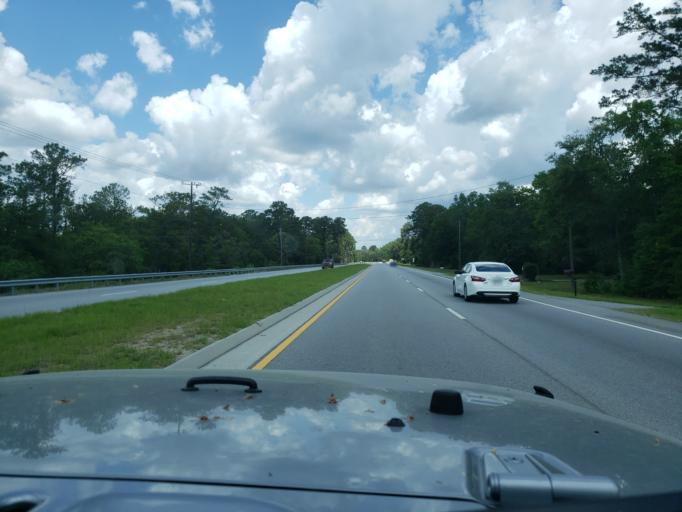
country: US
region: Georgia
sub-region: Chatham County
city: Georgetown
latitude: 32.0423
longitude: -81.2106
